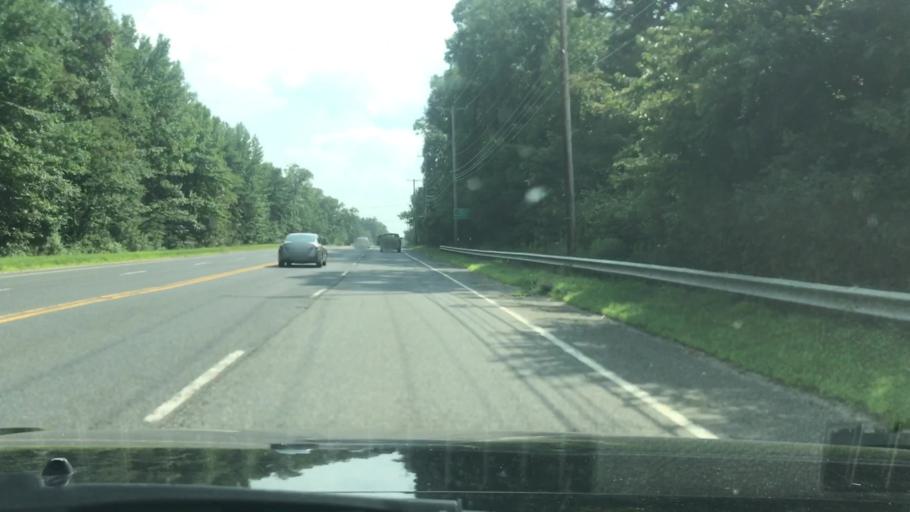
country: US
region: New Jersey
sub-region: Monmouth County
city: Farmingdale
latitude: 40.2345
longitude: -74.1103
